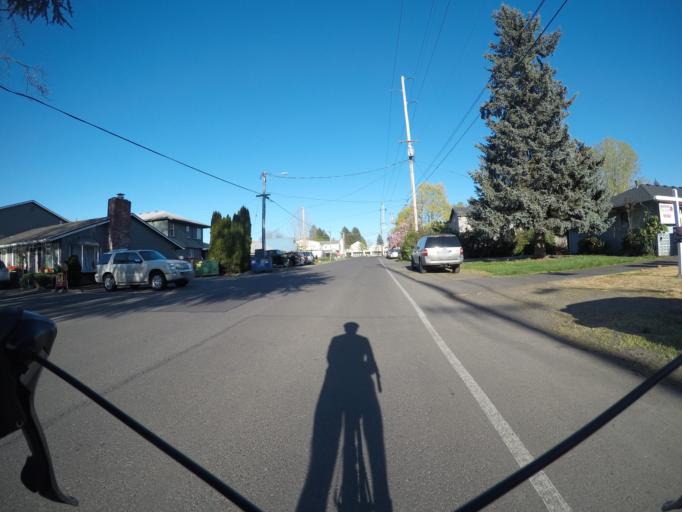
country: US
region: Oregon
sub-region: Washington County
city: Aloha
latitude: 45.4924
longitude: -122.8691
